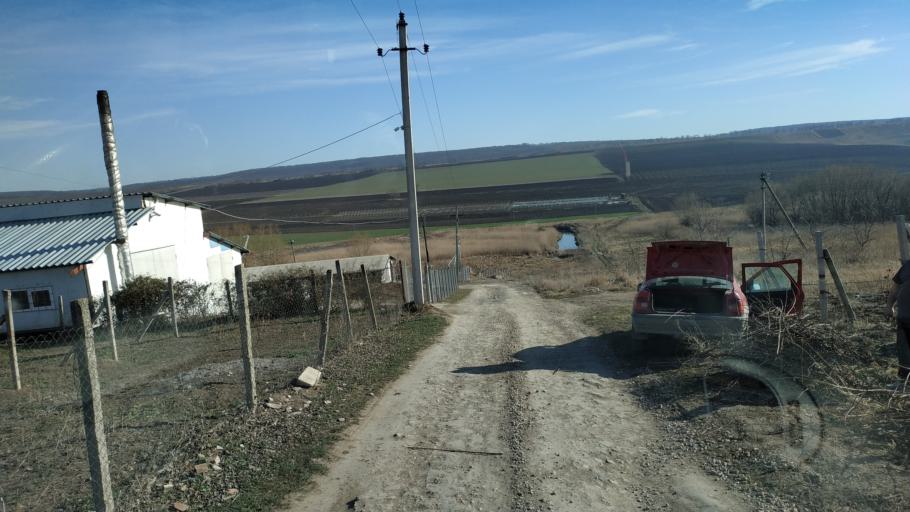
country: MD
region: Chisinau
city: Vatra
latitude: 47.0214
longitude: 28.6502
